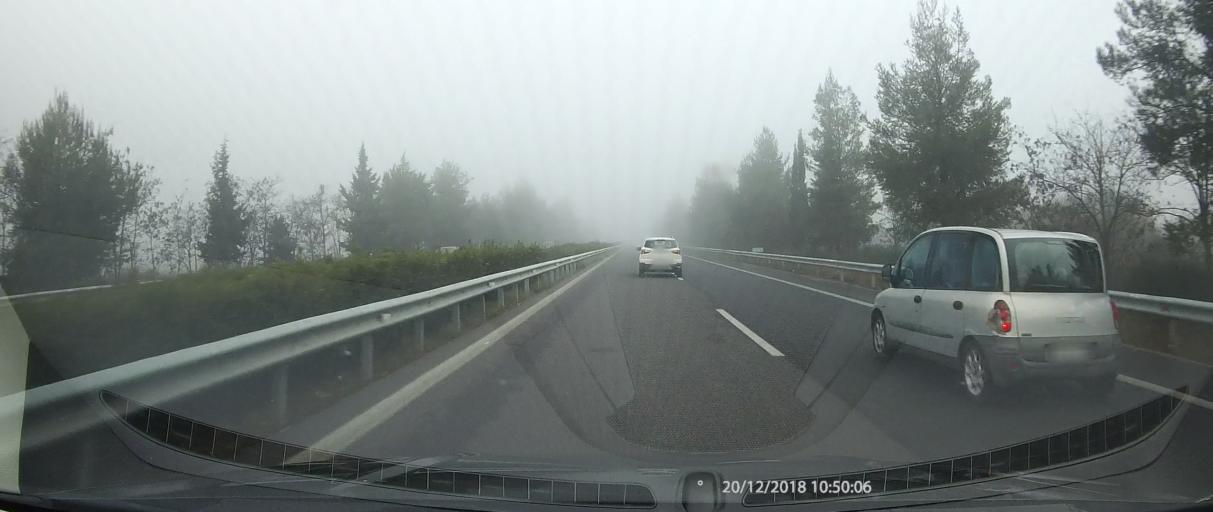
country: GR
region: Peloponnese
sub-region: Nomos Arkadias
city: Tripoli
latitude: 37.5553
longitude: 22.4215
